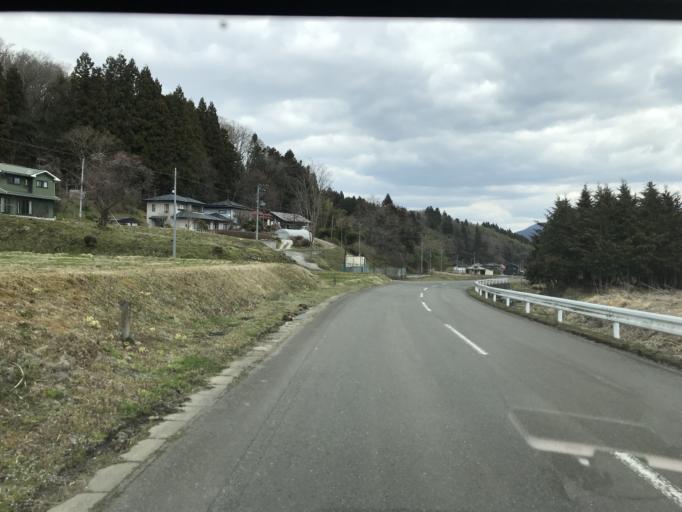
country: JP
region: Iwate
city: Ichinoseki
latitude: 38.9693
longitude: 141.0995
